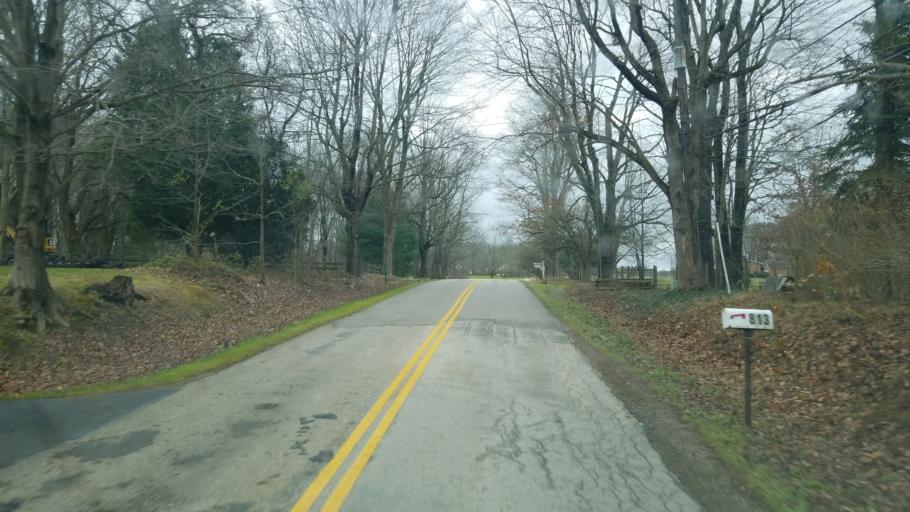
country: US
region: Ohio
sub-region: Ashtabula County
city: Roaming Shores
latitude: 41.6296
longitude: -80.8265
